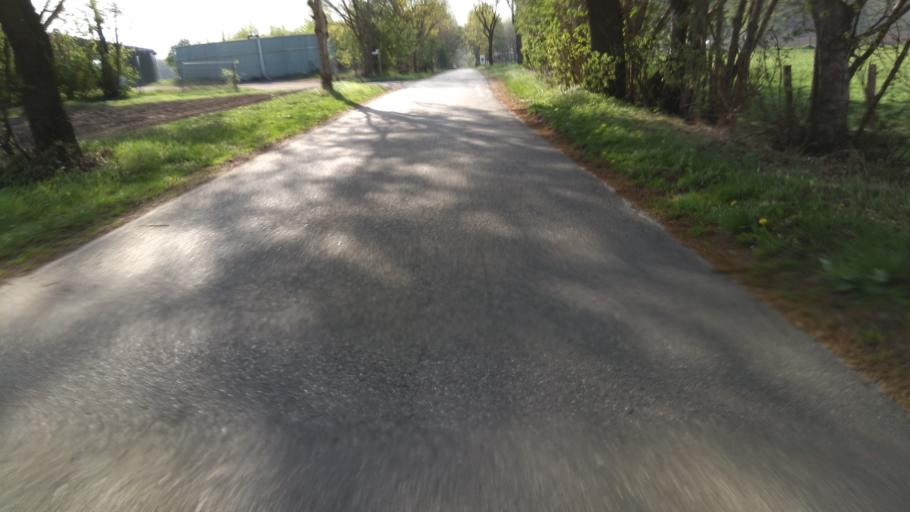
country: DE
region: Lower Saxony
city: Buxtehude
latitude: 53.4367
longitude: 9.6809
